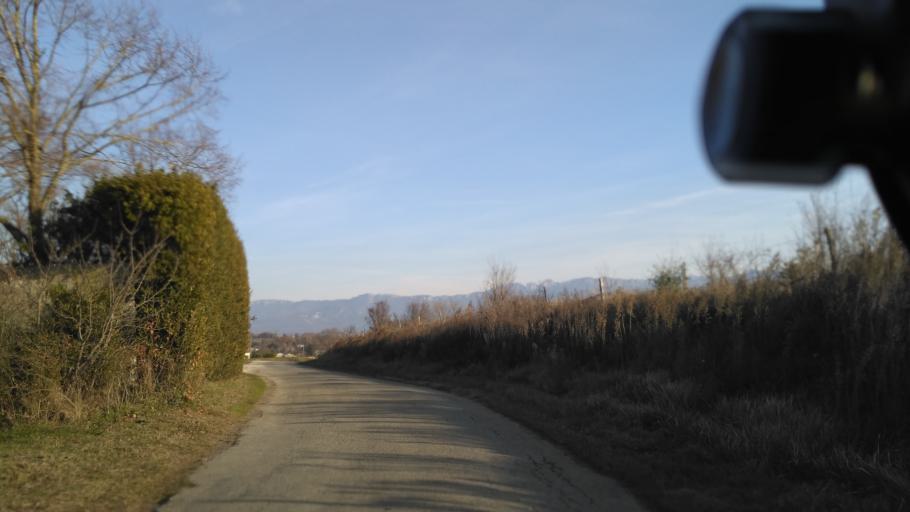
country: FR
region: Rhone-Alpes
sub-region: Departement de la Drome
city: Alixan
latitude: 44.9776
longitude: 5.0170
